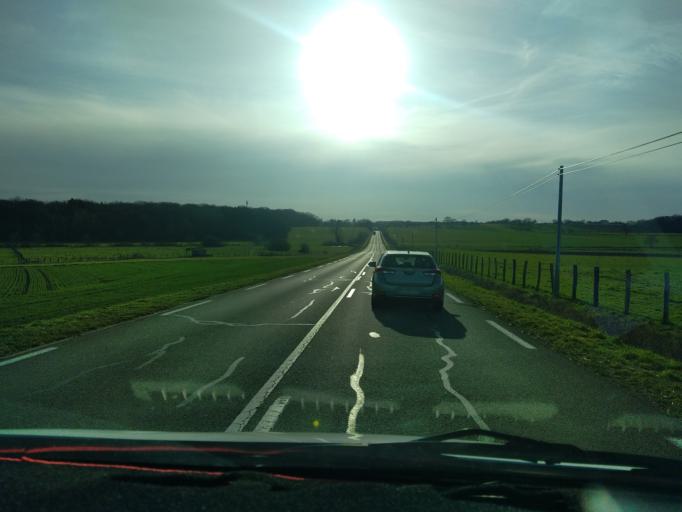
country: FR
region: Franche-Comte
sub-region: Departement de la Haute-Saone
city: Gray
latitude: 47.3711
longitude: 5.6671
